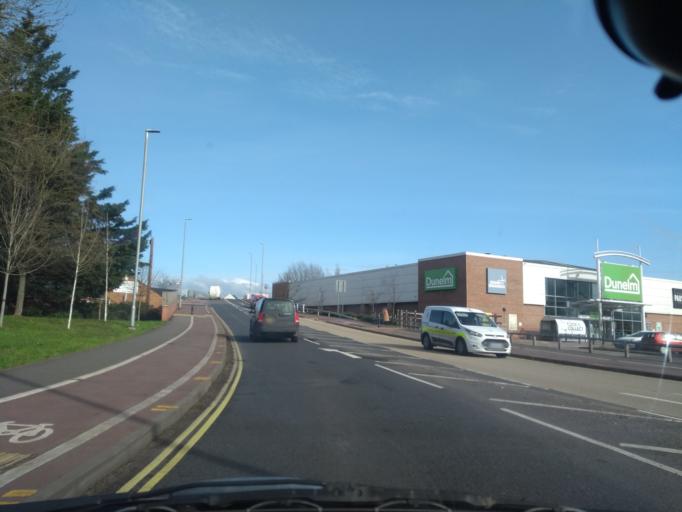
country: GB
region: England
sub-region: Somerset
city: Taunton
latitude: 51.0196
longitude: -3.0938
